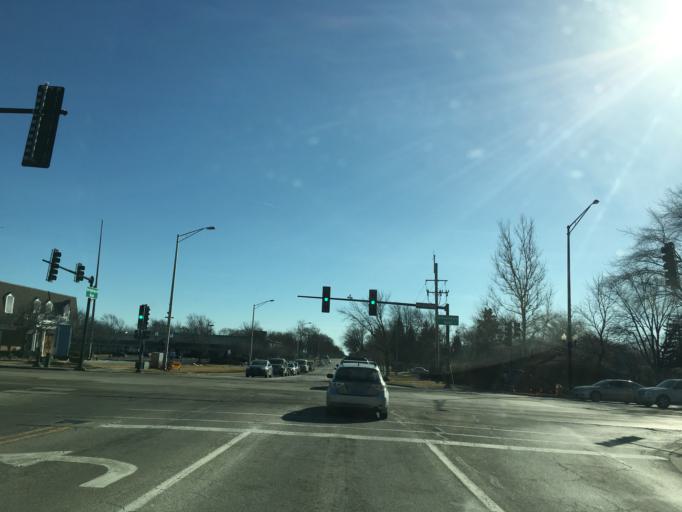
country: US
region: Illinois
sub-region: Cook County
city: Schaumburg
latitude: 42.0261
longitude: -88.1192
